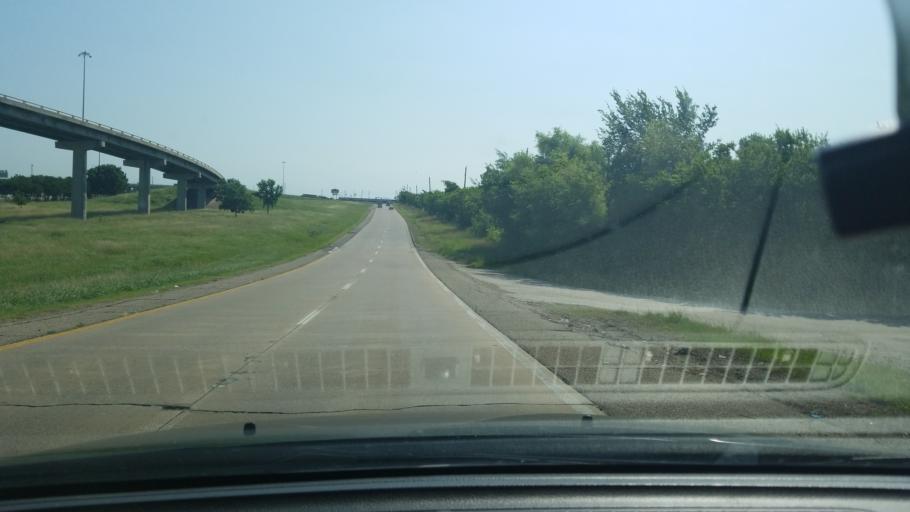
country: US
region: Texas
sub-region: Dallas County
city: Mesquite
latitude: 32.8223
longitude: -96.6287
